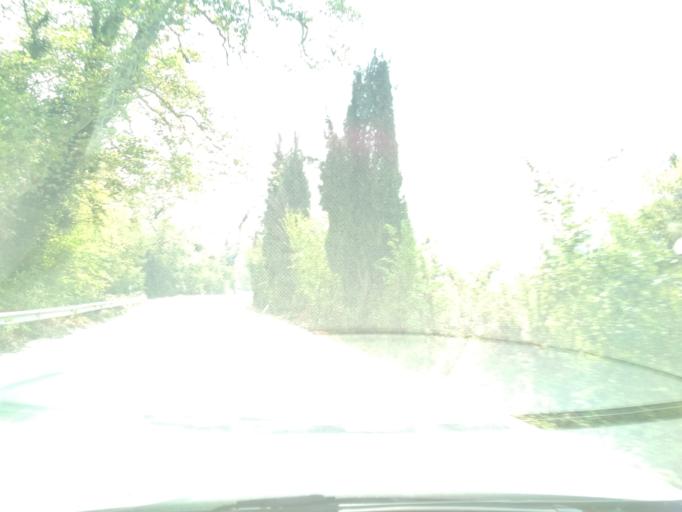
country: GR
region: Central Greece
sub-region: Nomos Evvoias
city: Prokopion
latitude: 38.7226
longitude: 23.5091
